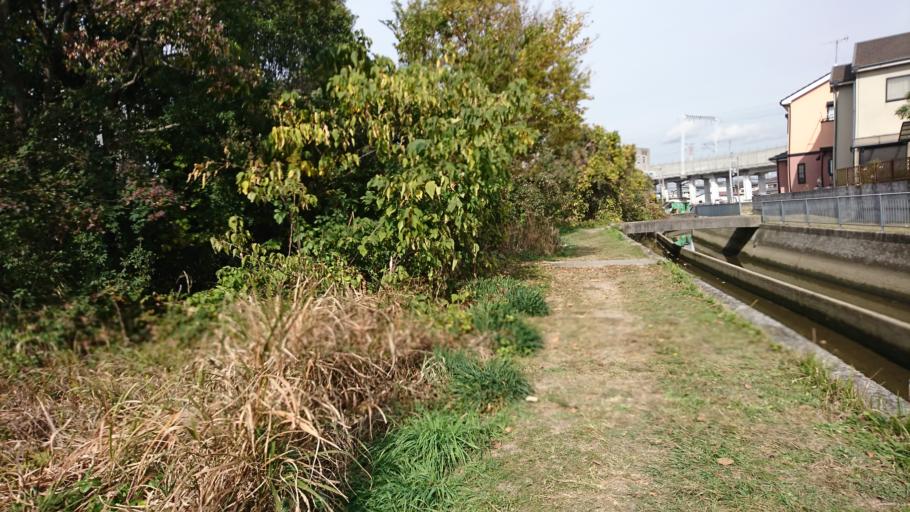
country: JP
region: Hyogo
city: Kakogawacho-honmachi
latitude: 34.7564
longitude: 134.8115
